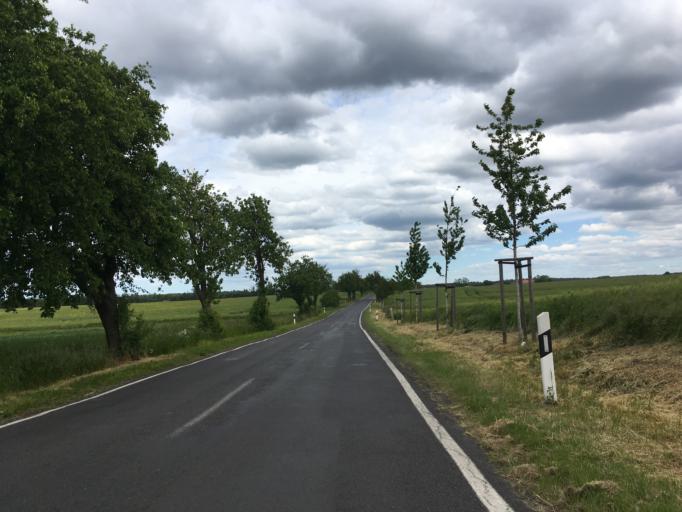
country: DE
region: Brandenburg
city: Hohenfinow
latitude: 52.7615
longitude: 13.8814
